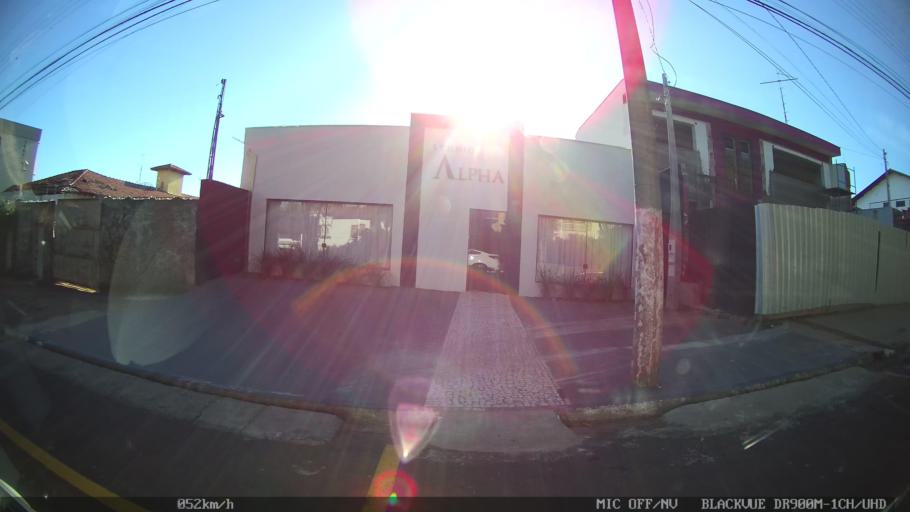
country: BR
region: Sao Paulo
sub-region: Franca
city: Franca
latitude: -20.5580
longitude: -47.4035
